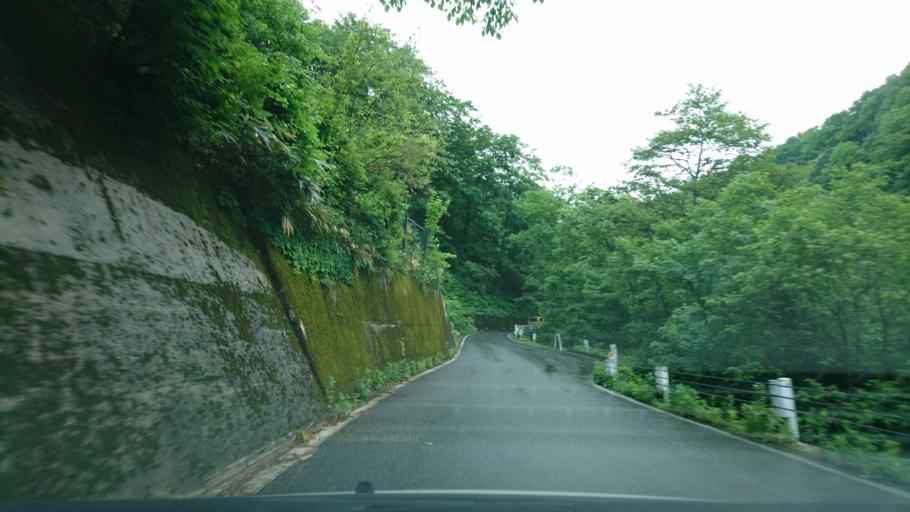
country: JP
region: Iwate
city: Ichinoseki
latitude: 38.9977
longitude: 140.8330
